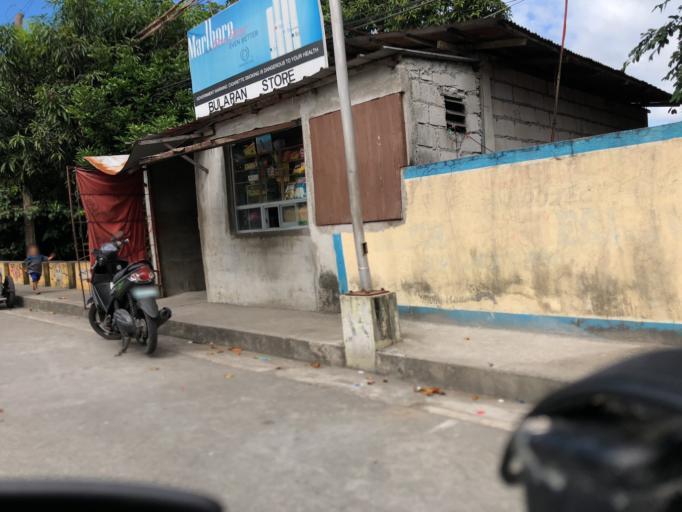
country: PH
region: Central Luzon
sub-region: Province of Bulacan
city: San Jose del Monte
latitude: 14.7623
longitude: 121.0502
